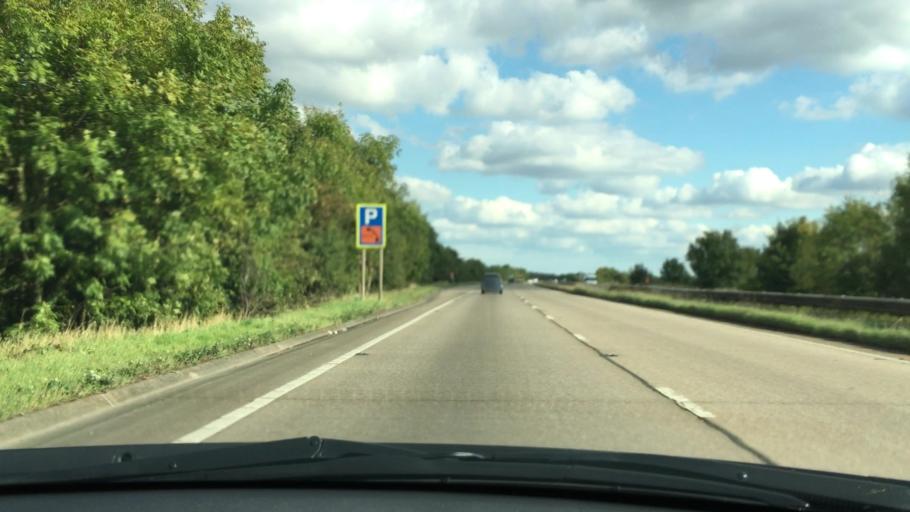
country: GB
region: England
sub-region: North East Lincolnshire
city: Healing
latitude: 53.5937
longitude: -0.1719
